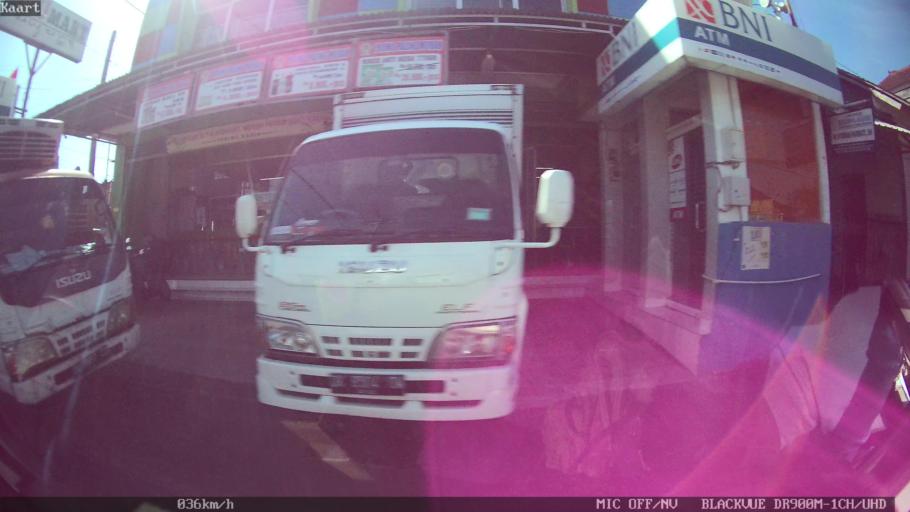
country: ID
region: Bali
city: Banjar Kertasari
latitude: -8.6308
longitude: 115.1849
